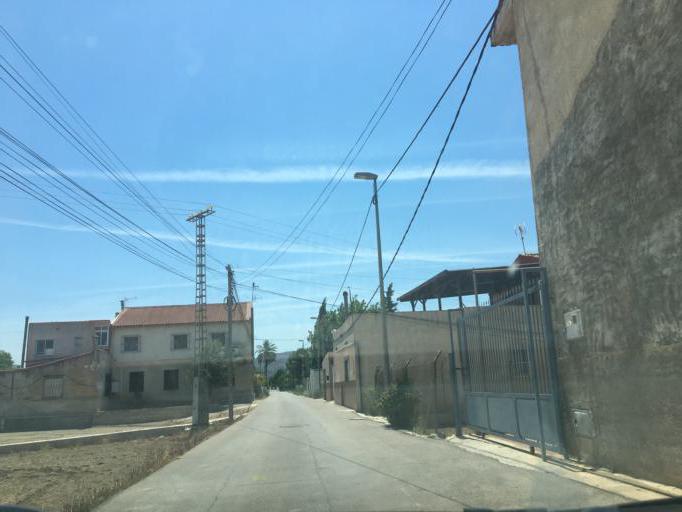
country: ES
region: Murcia
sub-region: Murcia
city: Santomera
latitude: 38.0200
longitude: -1.0568
